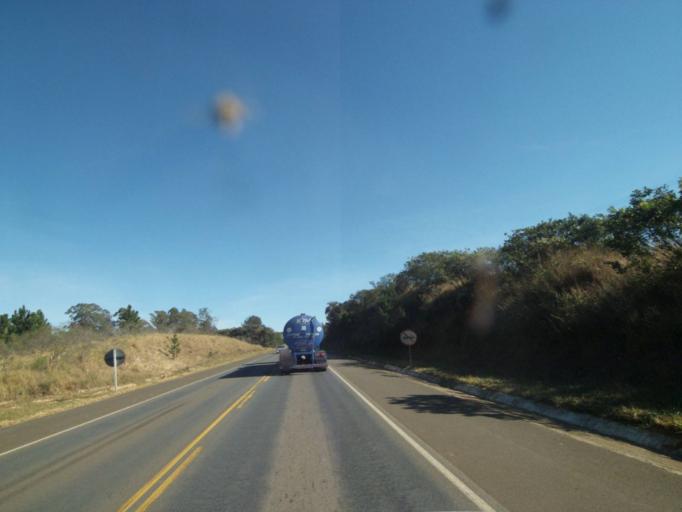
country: BR
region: Parana
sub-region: Tibagi
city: Tibagi
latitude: -24.4915
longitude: -50.4409
